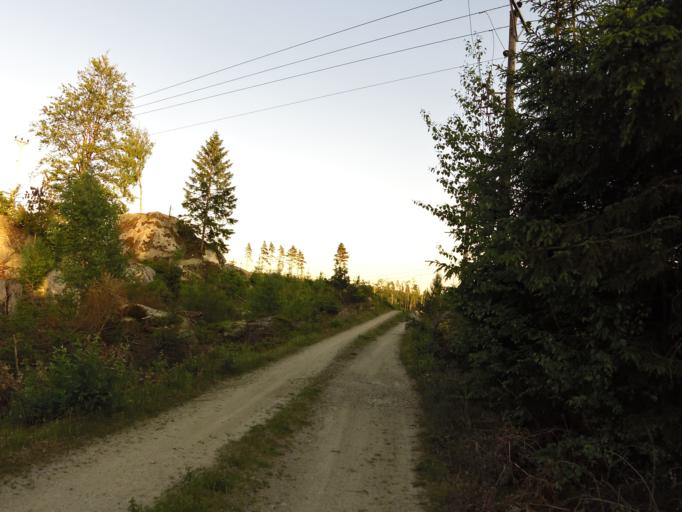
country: SE
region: Blekinge
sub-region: Olofstroms Kommun
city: Olofstroem
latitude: 56.4134
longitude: 14.5440
